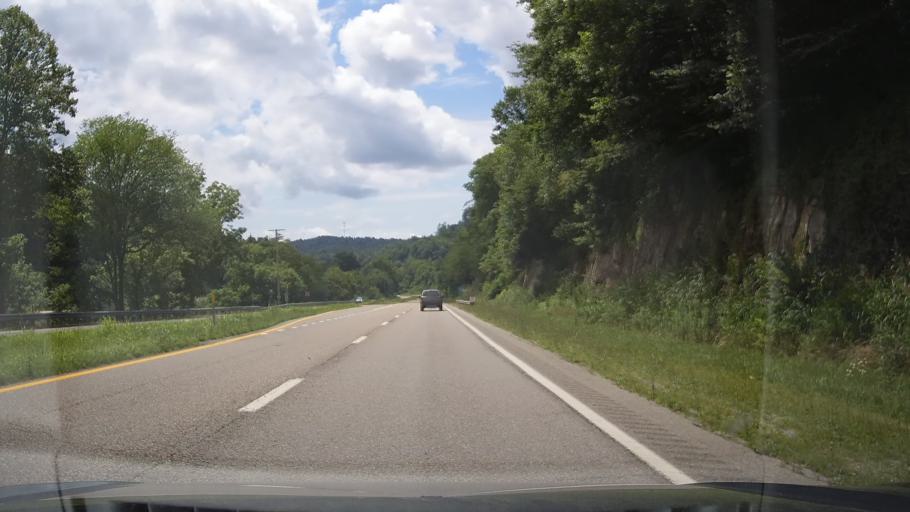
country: US
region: Tennessee
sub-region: Hawkins County
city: Mount Carmel
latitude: 36.6418
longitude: -82.7235
